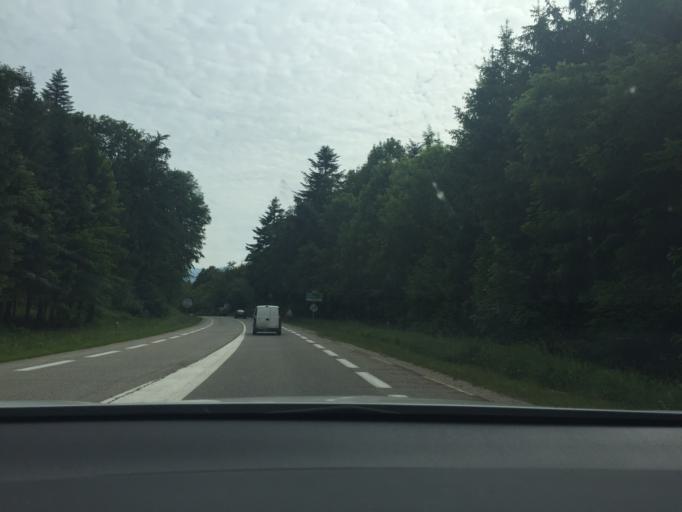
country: FR
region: Rhone-Alpes
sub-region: Departement de la Savoie
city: Les Echelles
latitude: 45.4688
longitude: 5.8164
